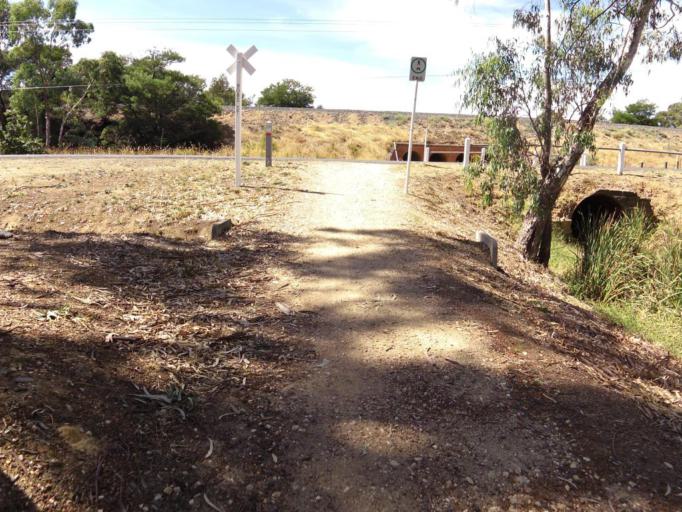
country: AU
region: Victoria
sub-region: Greater Bendigo
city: White Hills
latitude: -36.7428
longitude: 144.2976
